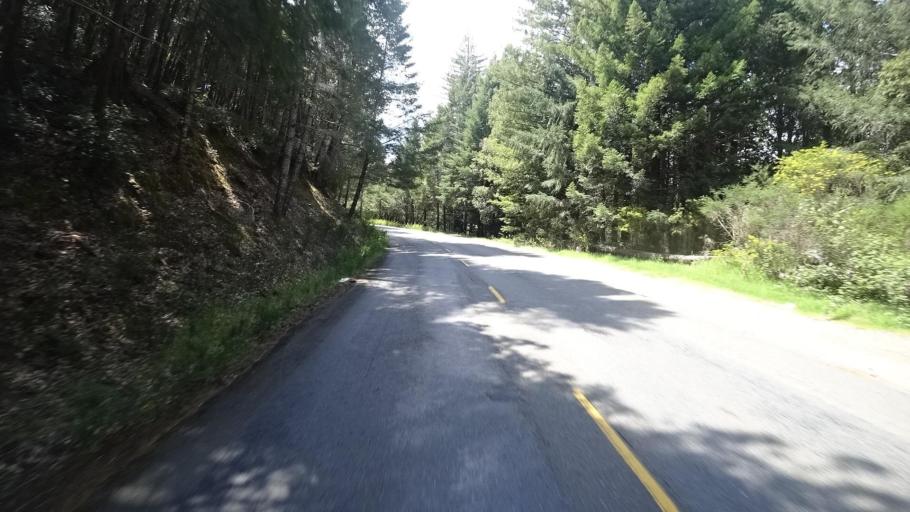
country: US
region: California
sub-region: Humboldt County
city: Redway
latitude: 40.0510
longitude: -123.9572
